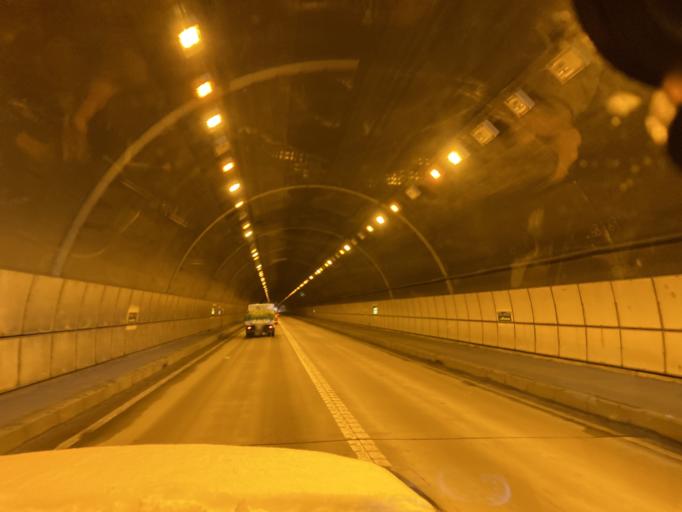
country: JP
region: Nagano
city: Nagano-shi
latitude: 36.6171
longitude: 138.1322
